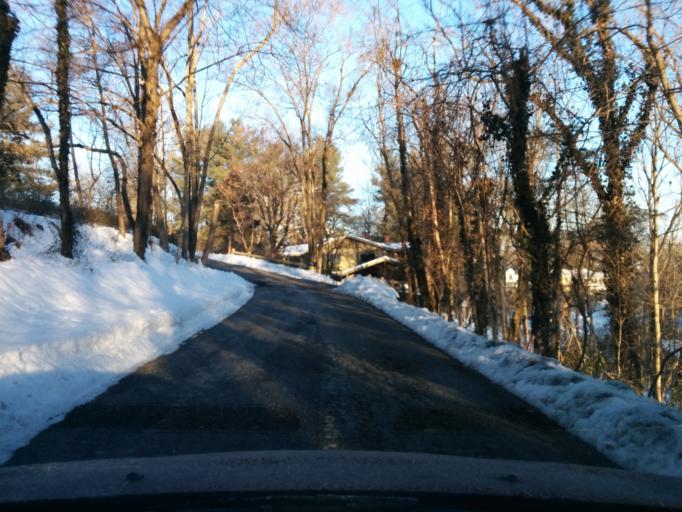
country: US
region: Virginia
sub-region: City of Lexington
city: Lexington
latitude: 37.7768
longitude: -79.4523
